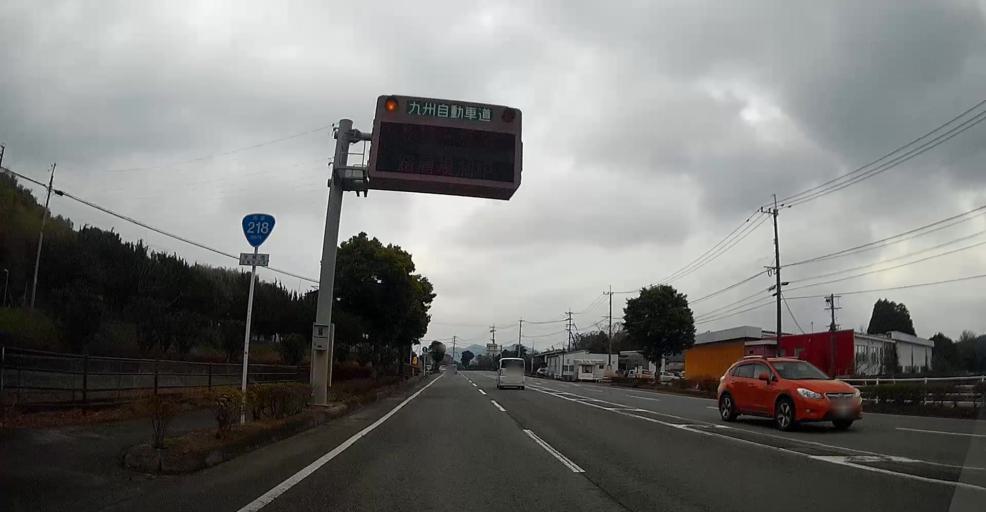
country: JP
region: Kumamoto
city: Matsubase
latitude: 32.6514
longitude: 130.7019
